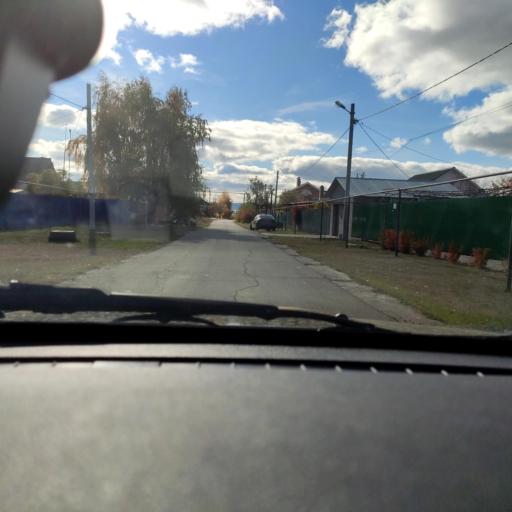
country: RU
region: Samara
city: Podstepki
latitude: 53.5104
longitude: 49.2352
